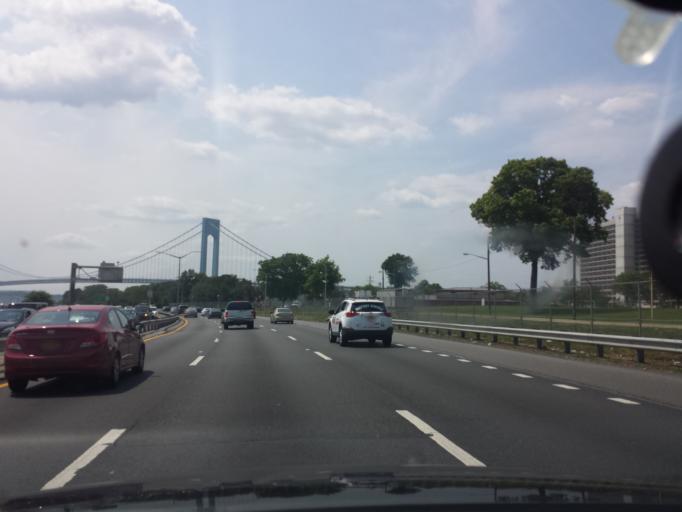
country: US
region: New York
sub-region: Kings County
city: Bensonhurst
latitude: 40.6045
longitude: -74.0213
